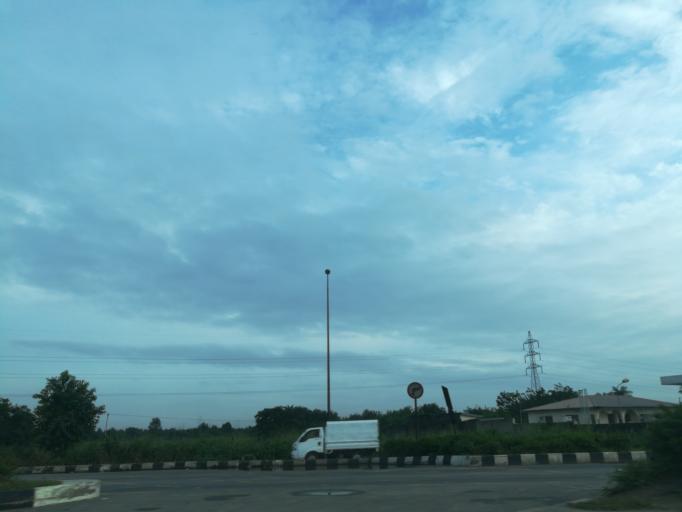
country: NG
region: Lagos
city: Ebute Ikorodu
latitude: 6.6154
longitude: 3.4445
